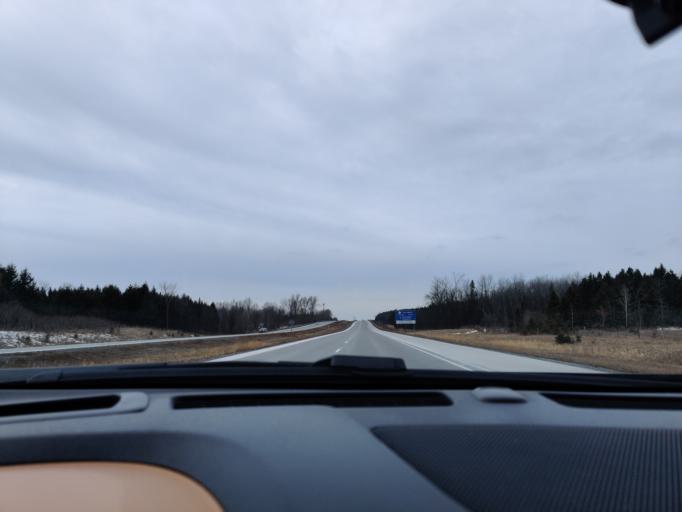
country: CA
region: Ontario
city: Cornwall
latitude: 45.0675
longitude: -74.6508
